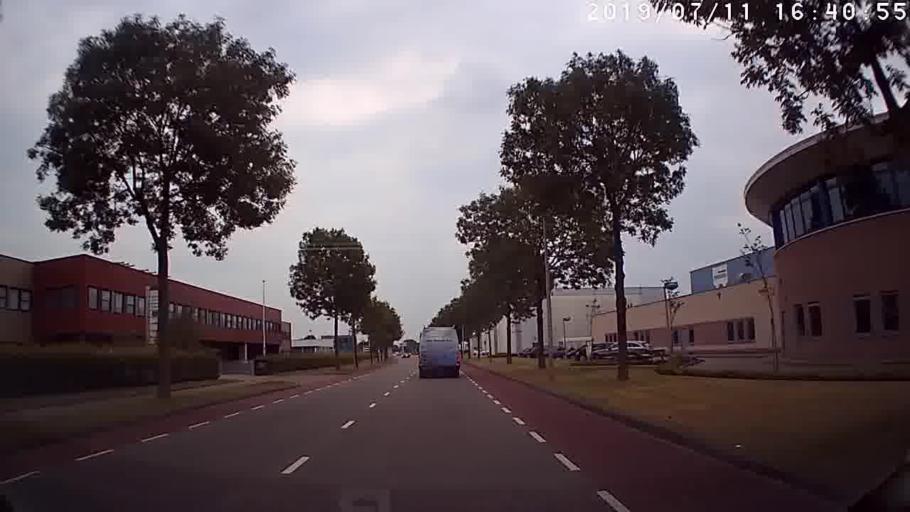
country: NL
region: Overijssel
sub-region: Gemeente Zwolle
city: Zwolle
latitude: 52.4942
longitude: 6.1251
